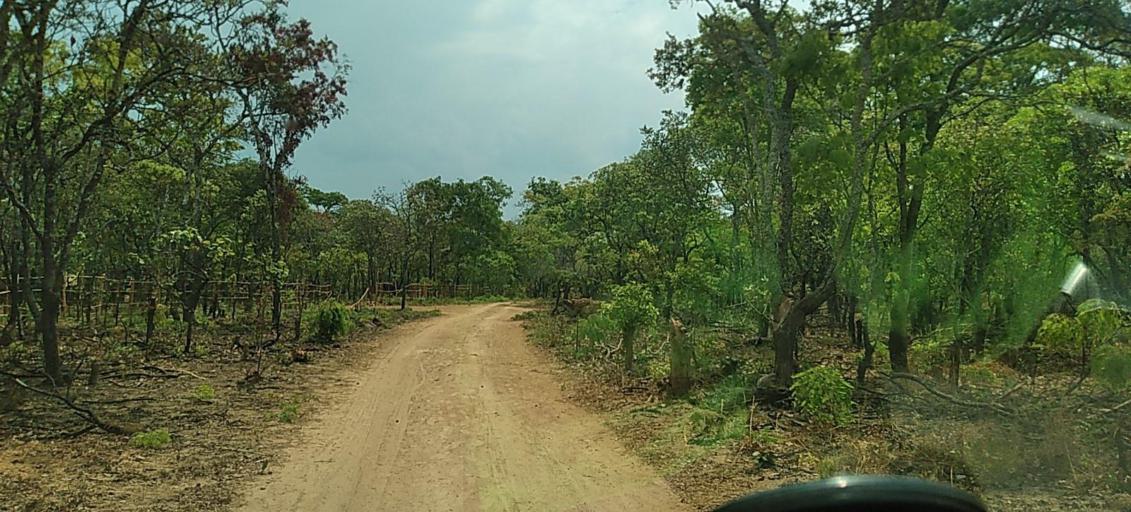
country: ZM
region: North-Western
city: Kansanshi
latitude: -12.0117
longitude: 26.2501
